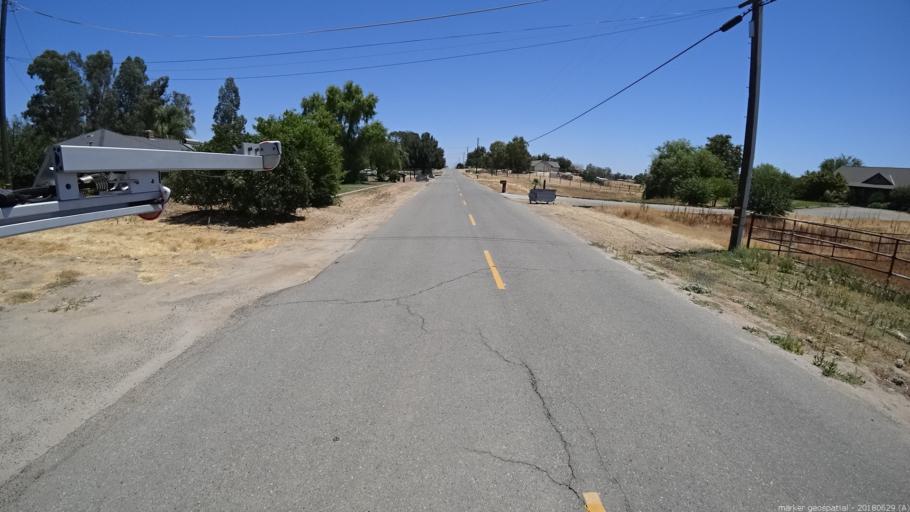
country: US
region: California
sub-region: Madera County
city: Parksdale
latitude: 36.9930
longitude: -119.9863
